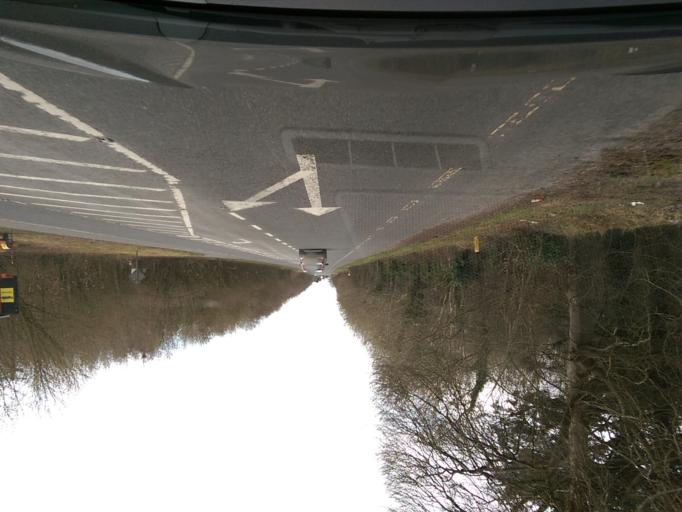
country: IE
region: Leinster
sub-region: An Iarmhi
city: Athlone
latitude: 53.3995
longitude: -7.8584
